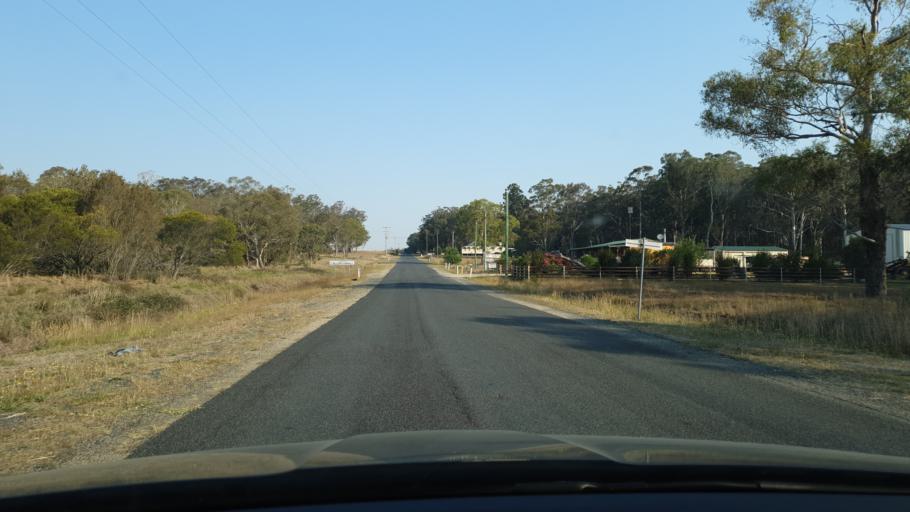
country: AU
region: New South Wales
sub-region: Tenterfield Municipality
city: Carrolls Creek
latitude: -28.6885
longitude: 152.0853
